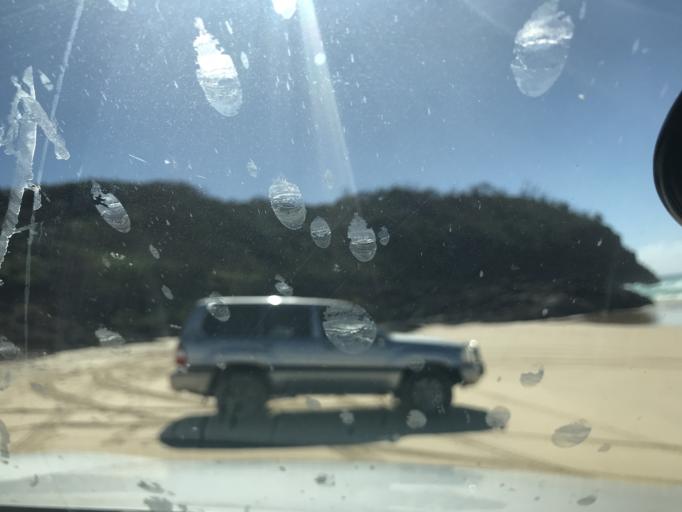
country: AU
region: Queensland
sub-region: Fraser Coast
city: Urangan
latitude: -25.0139
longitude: 153.3574
